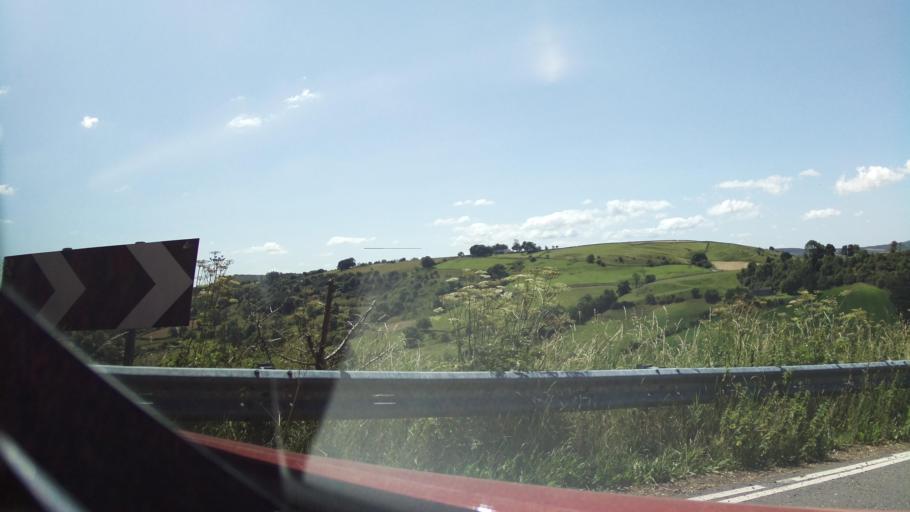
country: GB
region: England
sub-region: Derbyshire
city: Buxton
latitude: 53.1825
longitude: -1.8470
